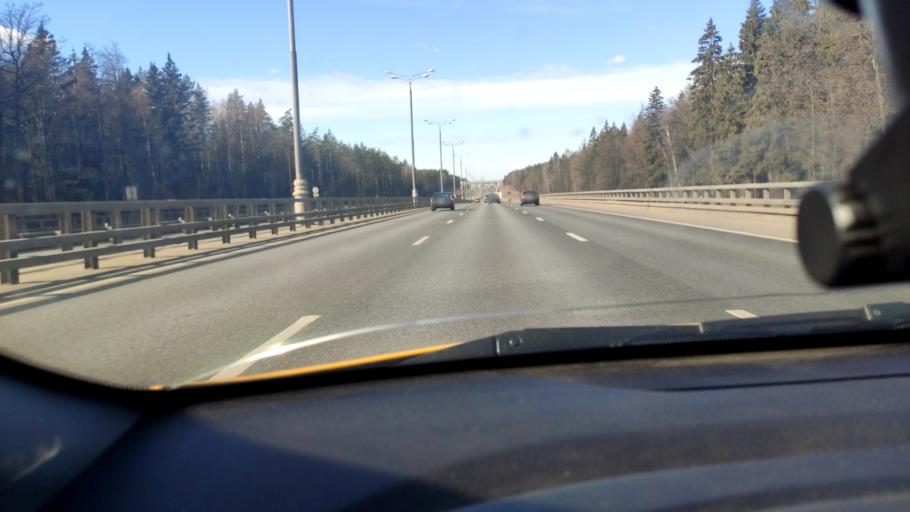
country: RU
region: Moskovskaya
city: Aprelevka
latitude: 55.5464
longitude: 37.1134
